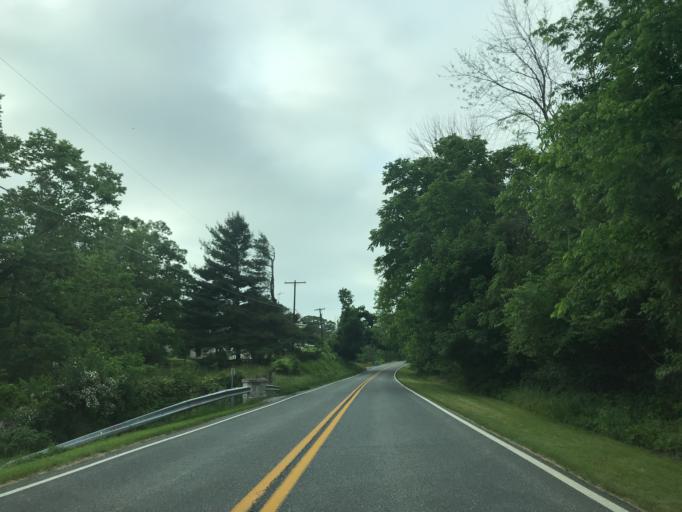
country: US
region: Maryland
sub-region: Frederick County
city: Clover Hill
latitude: 39.4981
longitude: -77.4023
